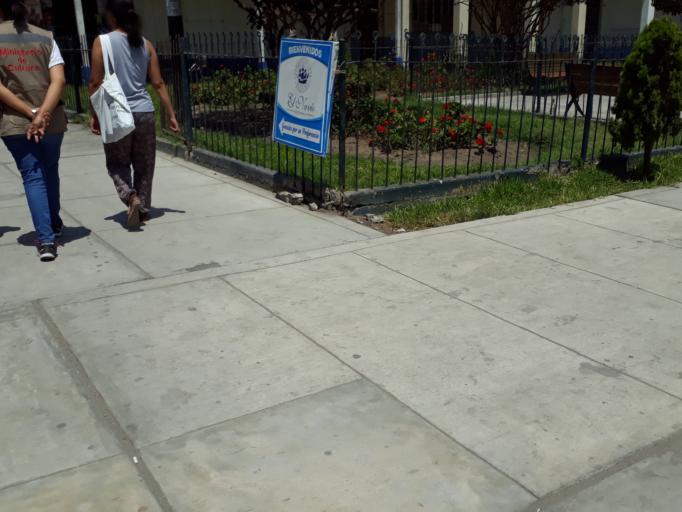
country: PE
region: Lima
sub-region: Lima
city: Santa Rosa
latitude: -11.7738
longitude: -77.1753
